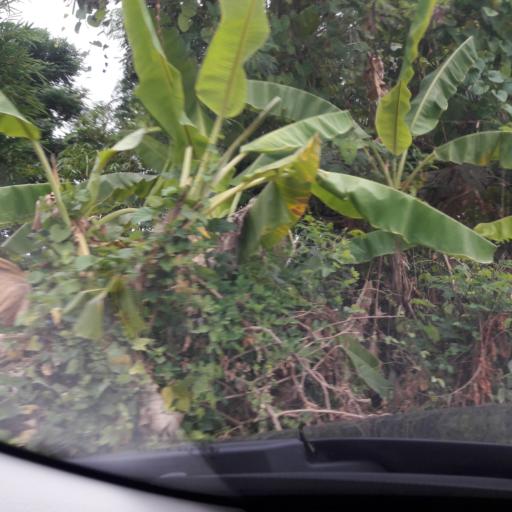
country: TH
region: Ratchaburi
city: Damnoen Saduak
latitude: 13.5749
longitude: 99.9456
